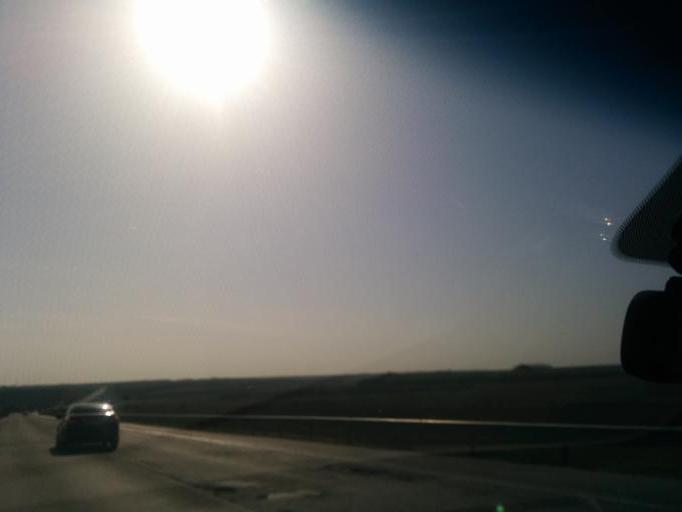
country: RU
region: Rostov
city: Mayskiy
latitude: 47.6582
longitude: 40.0425
